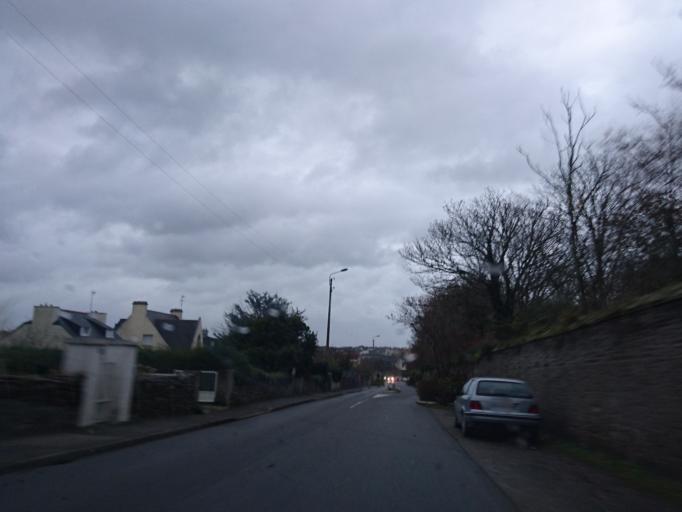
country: FR
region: Brittany
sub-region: Departement du Finistere
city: Le Conquet
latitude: 48.3606
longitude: -4.7690
